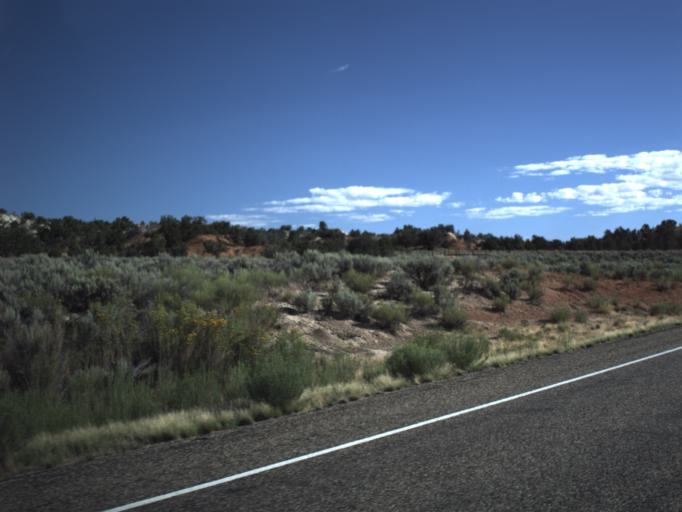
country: US
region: Utah
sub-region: Kane County
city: Kanab
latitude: 37.0668
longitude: -112.1807
